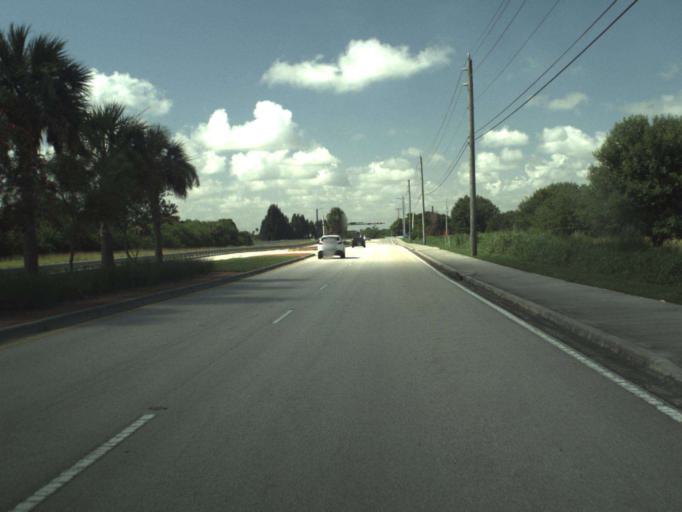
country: US
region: Florida
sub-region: Indian River County
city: Vero Beach South
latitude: 27.5910
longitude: -80.4475
